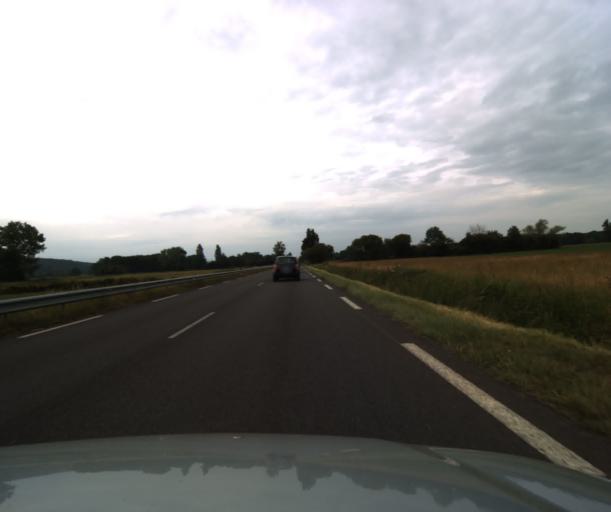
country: FR
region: Midi-Pyrenees
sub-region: Departement des Hautes-Pyrenees
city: Rabastens-de-Bigorre
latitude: 43.3463
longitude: 0.1351
